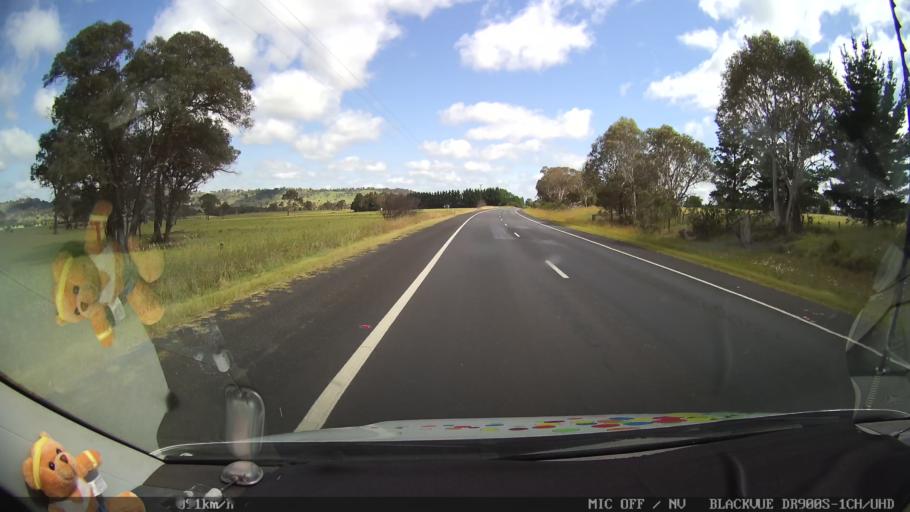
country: AU
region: New South Wales
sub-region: Glen Innes Severn
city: Glen Innes
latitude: -29.8797
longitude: 151.7340
